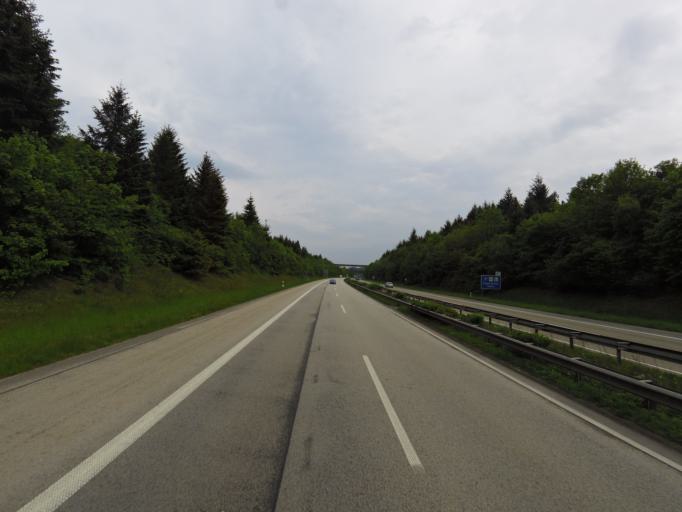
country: DE
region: Rheinland-Pfalz
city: Kratzenburg
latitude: 50.2127
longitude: 7.5585
